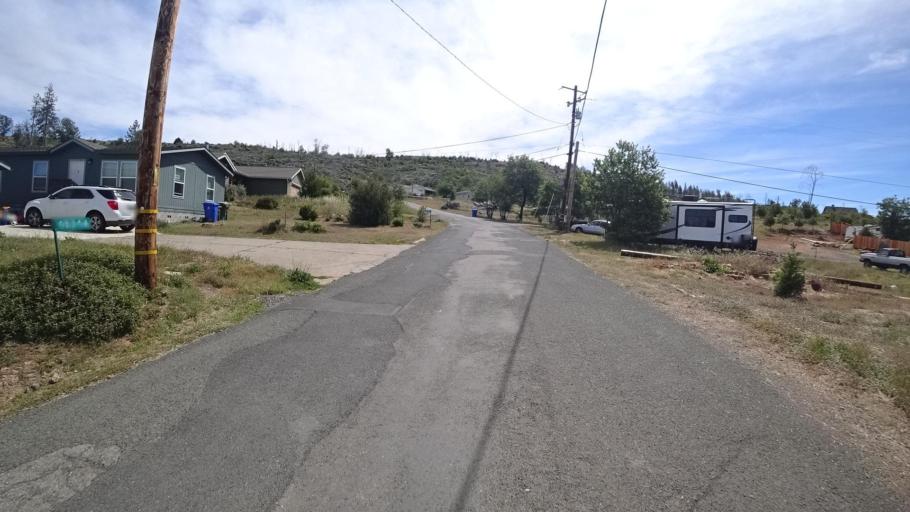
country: US
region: California
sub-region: Lake County
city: Cobb
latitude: 38.8393
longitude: -122.7275
